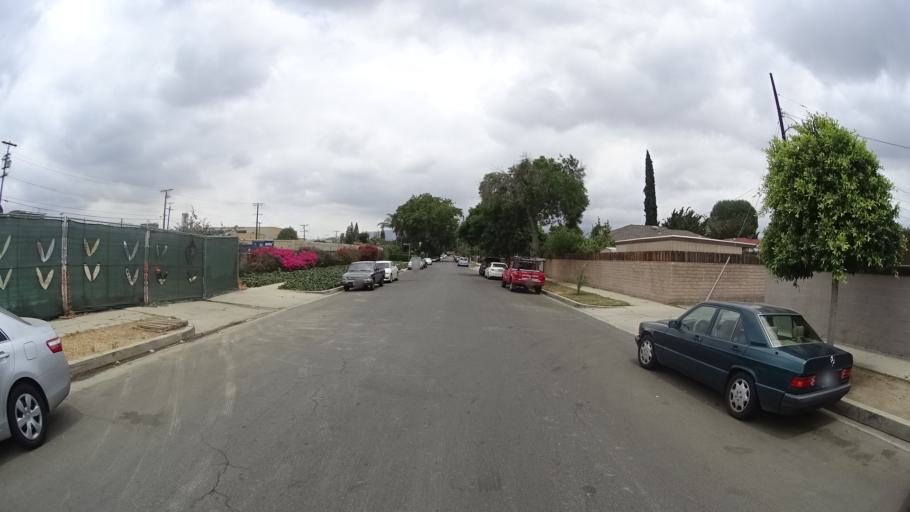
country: US
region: California
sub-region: Los Angeles County
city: San Fernando
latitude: 34.2577
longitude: -118.4650
